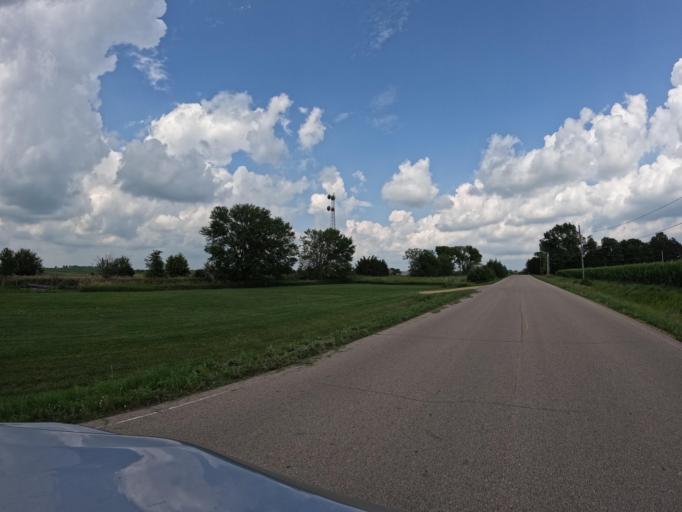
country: US
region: Iowa
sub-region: Clinton County
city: Camanche
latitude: 41.8011
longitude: -90.3467
